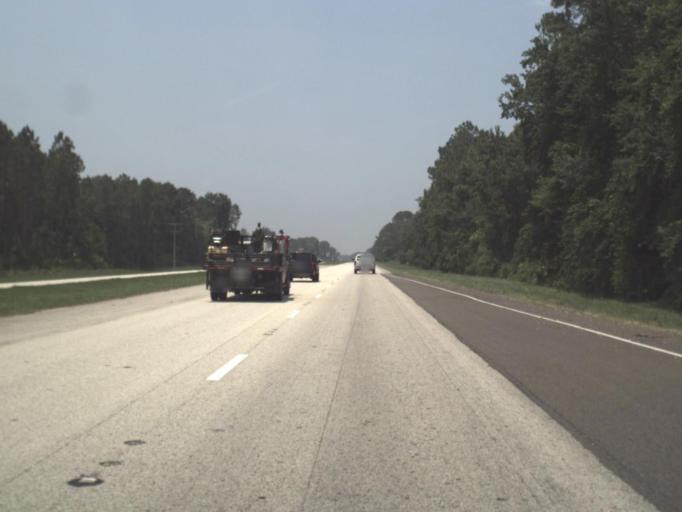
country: US
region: Florida
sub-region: Baker County
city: Macclenny
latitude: 30.1557
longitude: -82.0314
